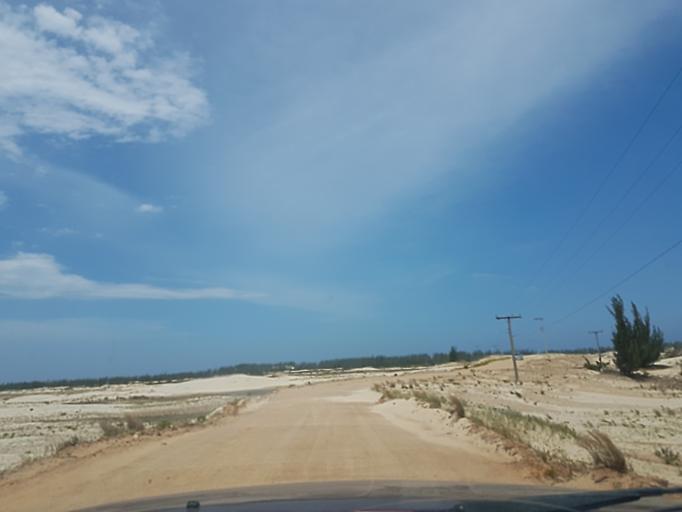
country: BR
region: Santa Catarina
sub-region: Jaguaruna
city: Jaguaruna
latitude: -28.6517
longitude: -48.9594
